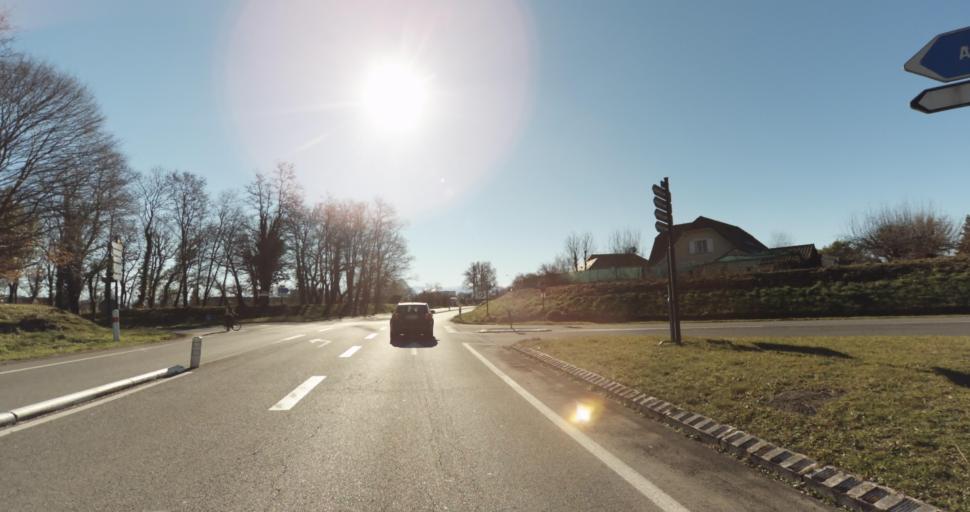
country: FR
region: Aquitaine
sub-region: Departement des Pyrenees-Atlantiques
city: Morlaas
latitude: 43.3407
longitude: -0.2508
